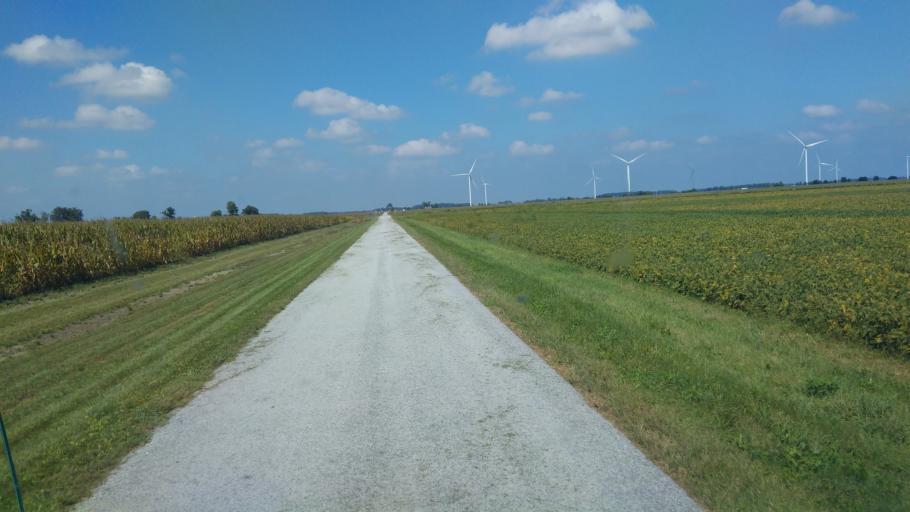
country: US
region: Ohio
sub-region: Hardin County
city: Ada
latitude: 40.7695
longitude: -83.7479
